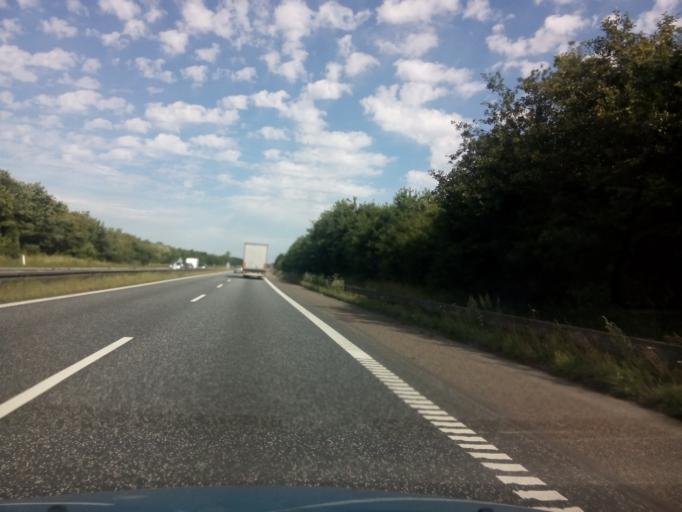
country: DK
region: Central Jutland
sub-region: Favrskov Kommune
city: Hadsten
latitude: 56.3492
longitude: 10.1181
